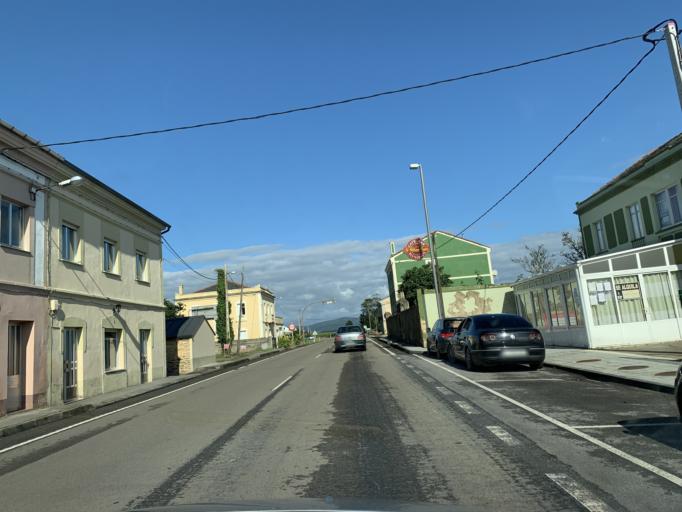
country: ES
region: Galicia
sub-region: Provincia de Lugo
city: Barreiros
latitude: 43.5451
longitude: -7.1954
